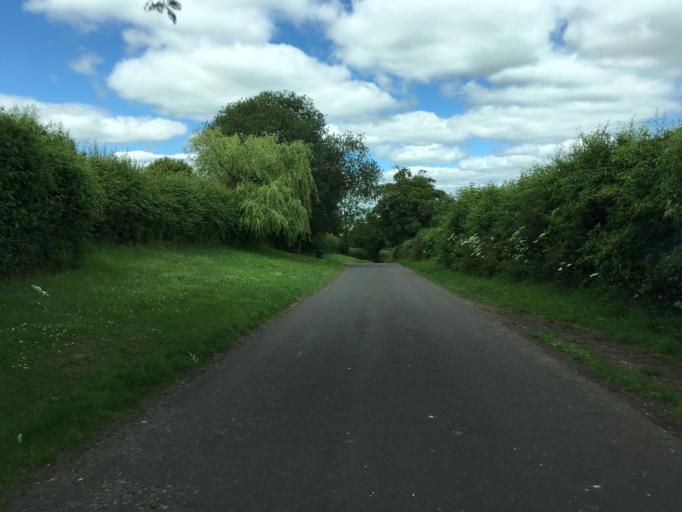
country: GB
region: England
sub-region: Hampshire
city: Highclere
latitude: 51.2733
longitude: -1.4206
